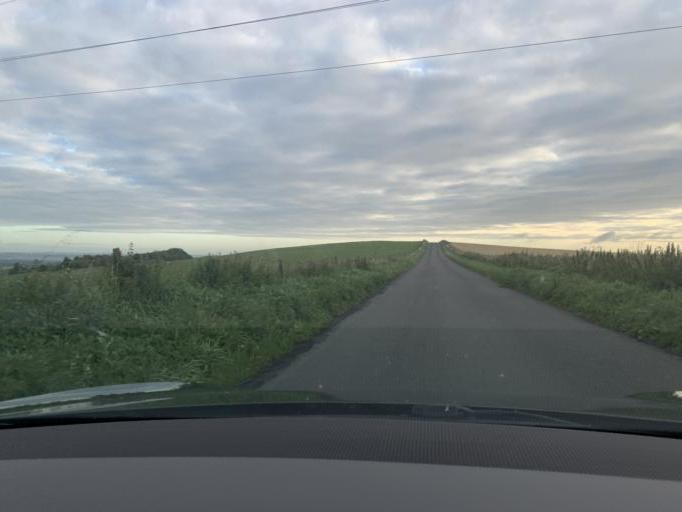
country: GB
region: England
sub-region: Wiltshire
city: Collingbourne Kingston
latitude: 51.3173
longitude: -1.6222
